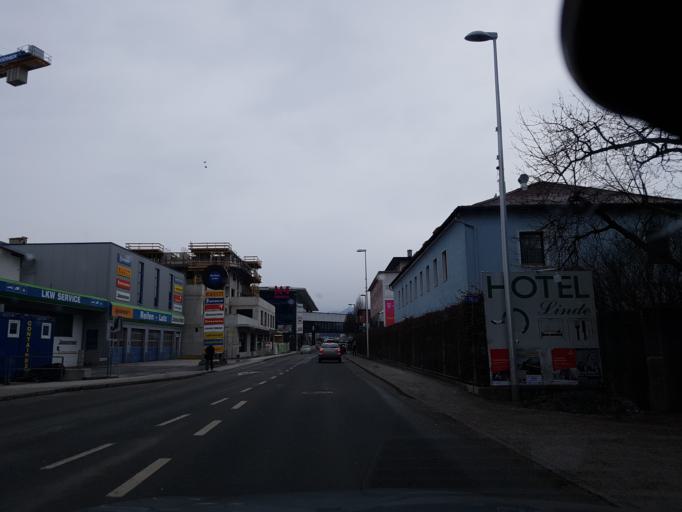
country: AT
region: Tyrol
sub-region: Politischer Bezirk Kufstein
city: Worgl
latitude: 47.4875
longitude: 12.0683
